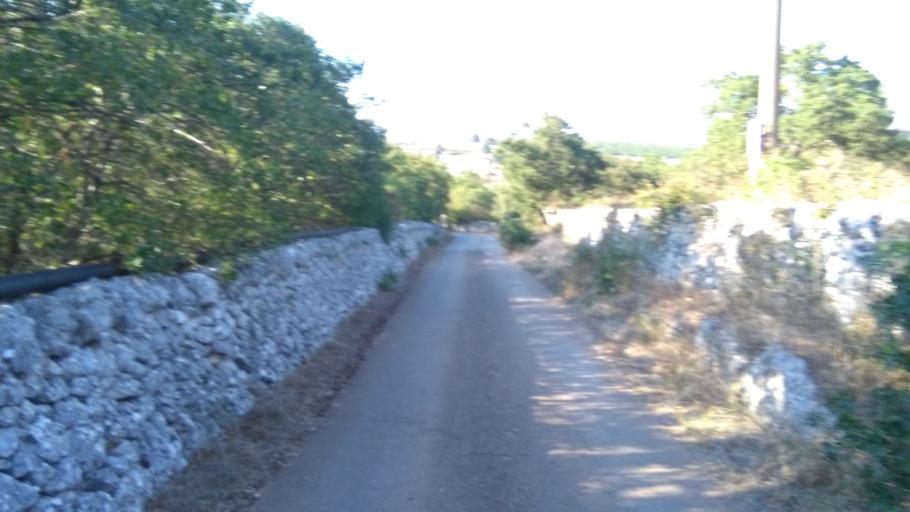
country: IT
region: Apulia
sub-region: Provincia di Bari
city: Putignano
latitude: 40.8262
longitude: 17.0590
